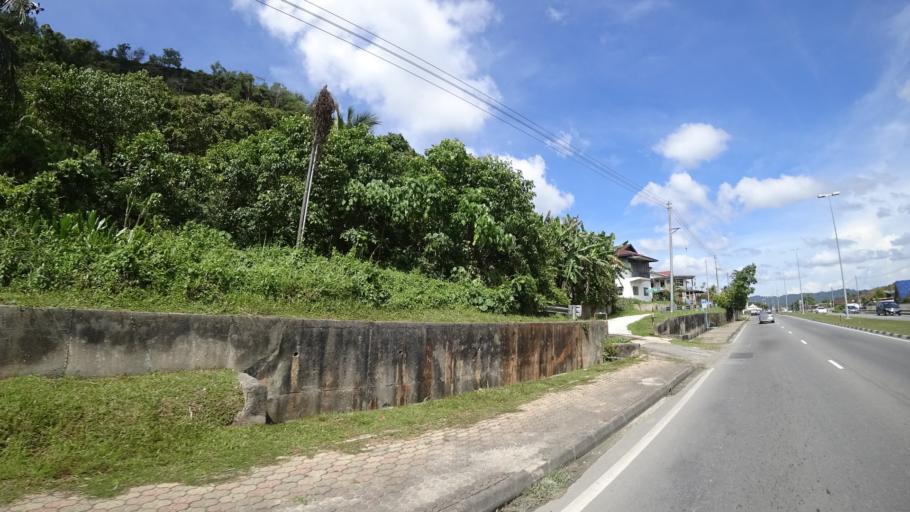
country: BN
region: Brunei and Muara
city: Bandar Seri Begawan
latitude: 4.8524
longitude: 114.8807
